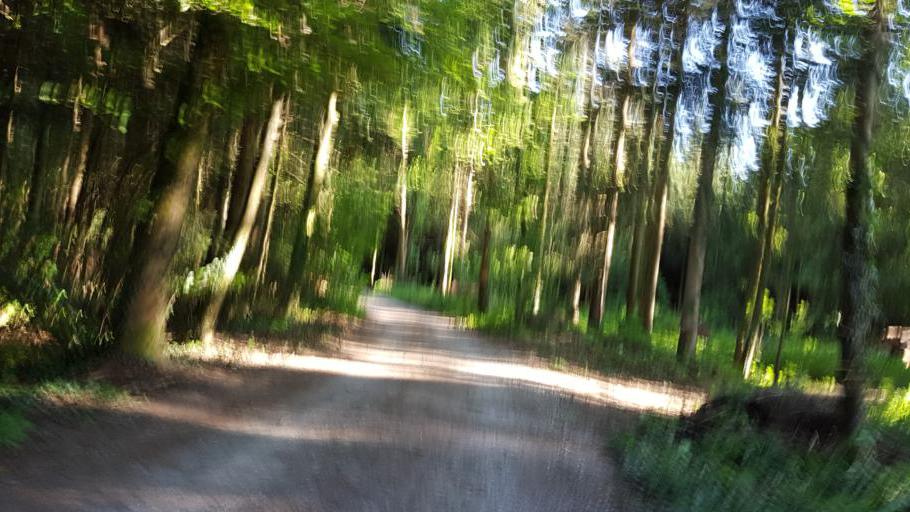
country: CH
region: Bern
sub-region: Bern-Mittelland District
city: Rubigen
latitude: 46.8973
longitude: 7.5571
